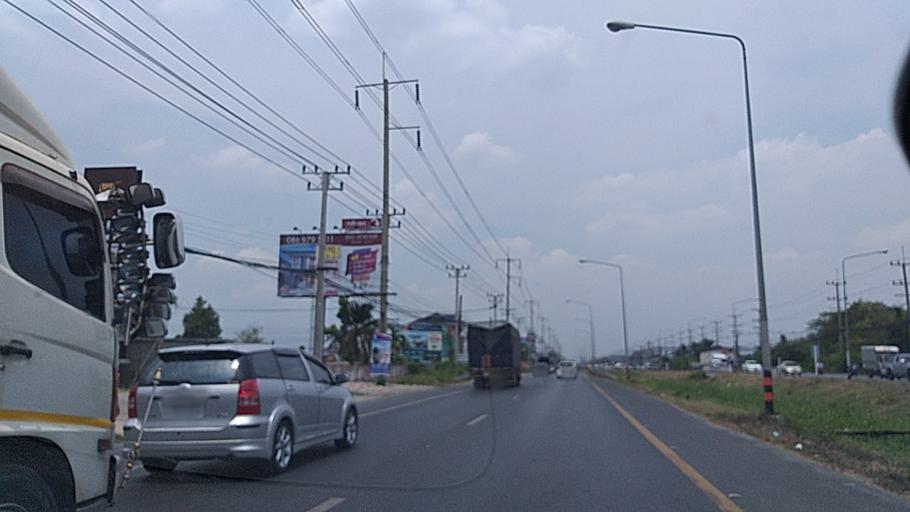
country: TH
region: Nakhon Pathom
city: Salaya
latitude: 13.7727
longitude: 100.3018
